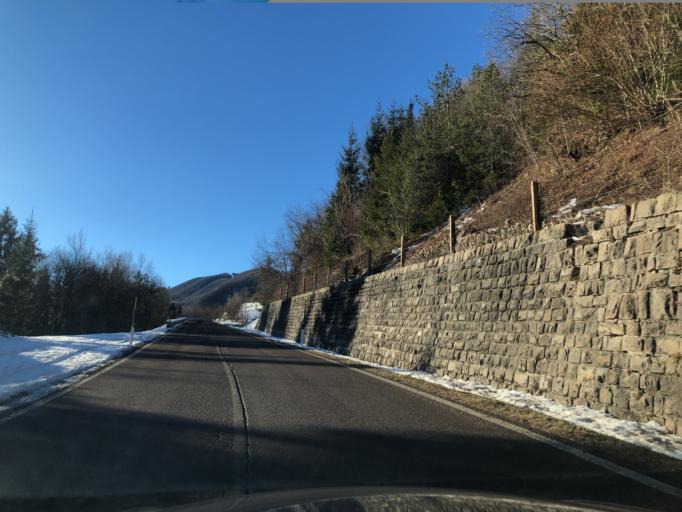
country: IT
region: Trentino-Alto Adige
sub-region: Provincia di Trento
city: Brentonico
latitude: 45.8025
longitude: 10.9321
